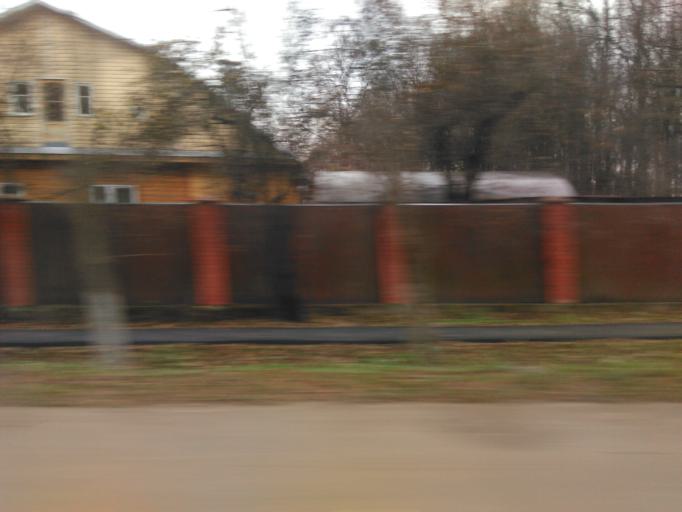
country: RU
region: Moskovskaya
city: Ashukino
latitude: 56.1598
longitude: 37.9519
